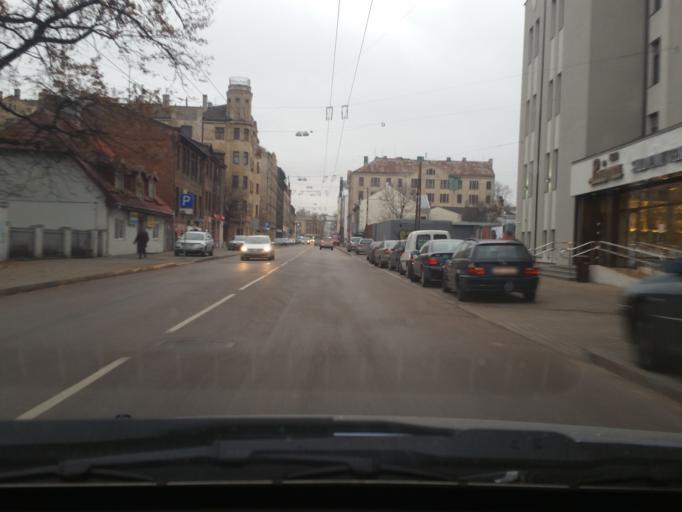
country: LV
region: Riga
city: Riga
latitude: 56.9579
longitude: 24.1458
